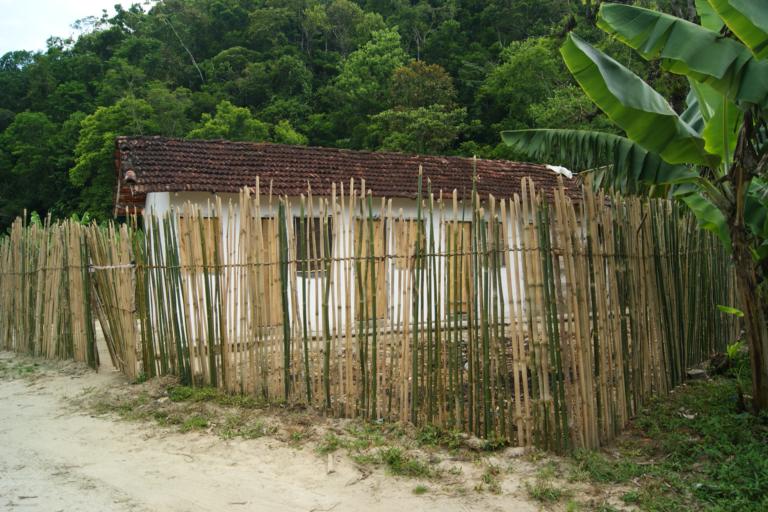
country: BR
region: Sao Paulo
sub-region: Mongagua
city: Mongagua
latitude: -24.0268
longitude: -46.7056
